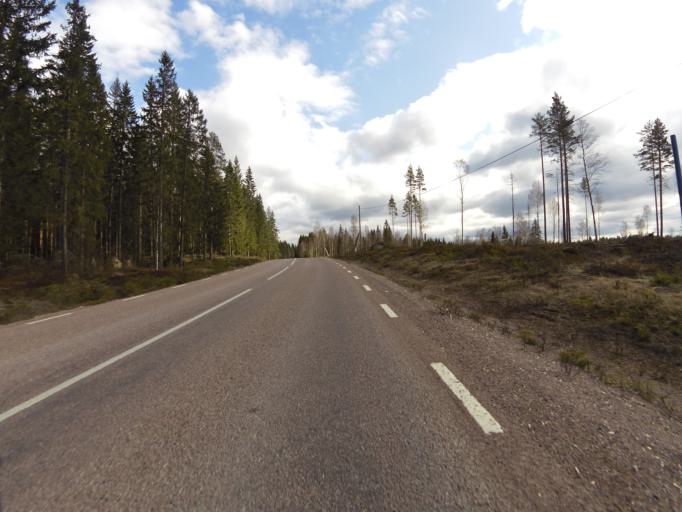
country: SE
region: Dalarna
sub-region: Avesta Kommun
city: Horndal
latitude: 60.3081
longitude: 16.2402
